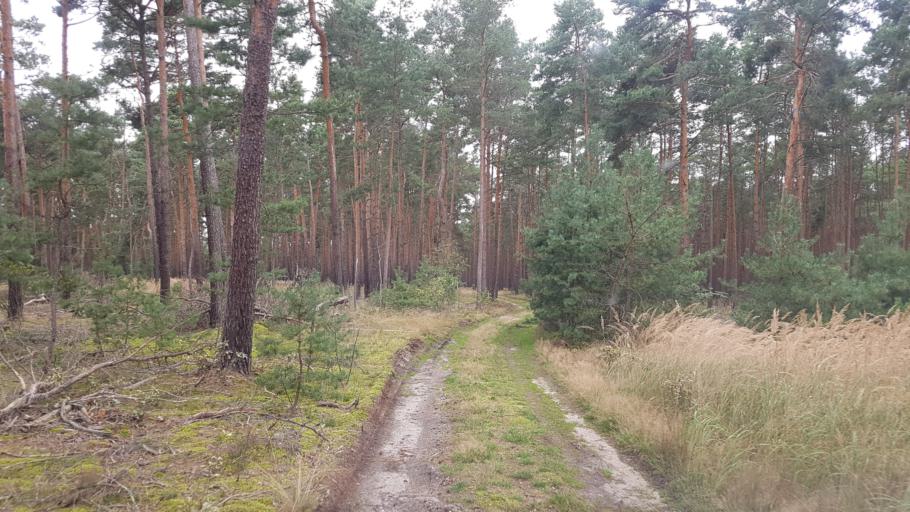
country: DE
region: Brandenburg
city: Doberlug-Kirchhain
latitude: 51.6128
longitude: 13.6114
